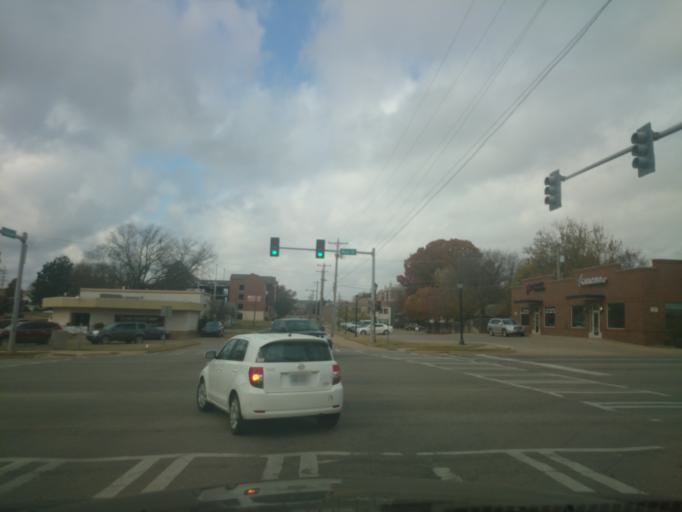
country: US
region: Oklahoma
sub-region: Payne County
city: Stillwater
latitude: 36.1238
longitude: -97.0585
